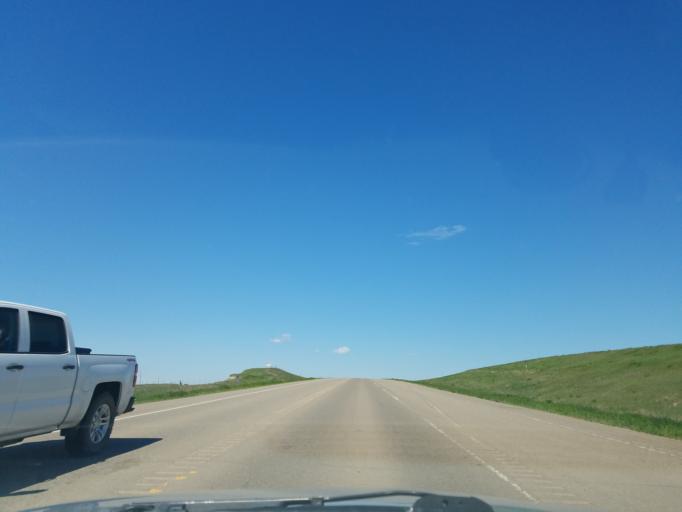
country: US
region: North Dakota
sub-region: McKenzie County
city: Watford City
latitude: 47.8034
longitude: -103.3406
